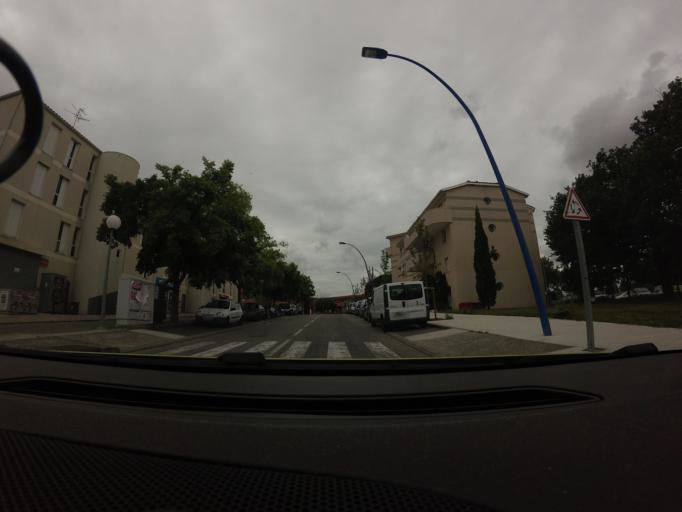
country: FR
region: Midi-Pyrenees
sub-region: Departement de la Haute-Garonne
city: Colomiers
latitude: 43.6166
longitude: 1.3119
